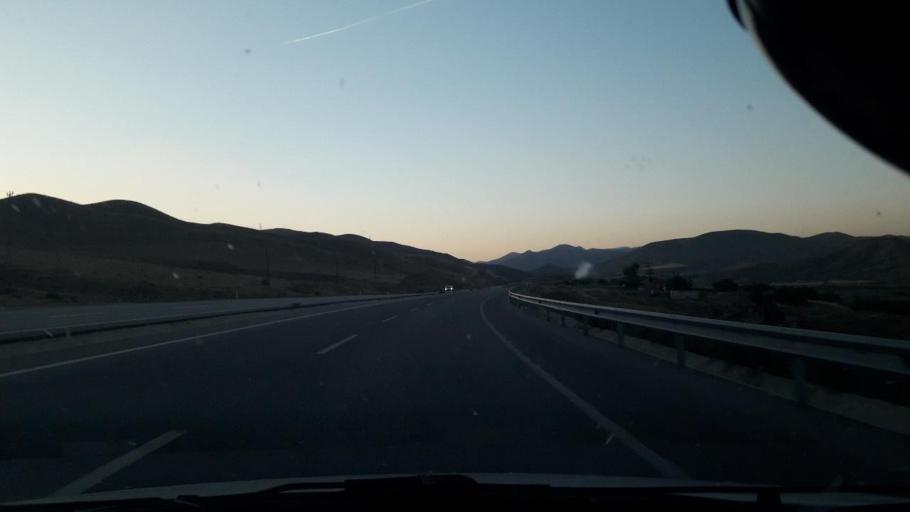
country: TR
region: Malatya
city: Yazihan
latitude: 38.6303
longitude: 38.1609
